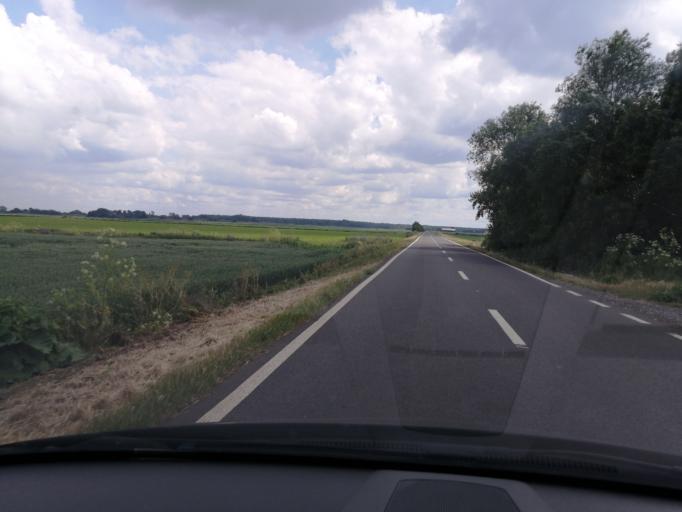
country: GB
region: England
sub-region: Cambridgeshire
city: Yaxley
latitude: 52.5057
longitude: -0.2561
